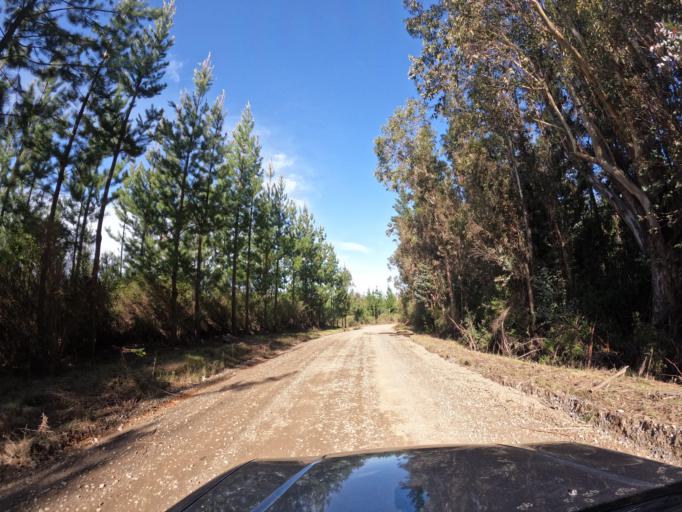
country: CL
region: Biobio
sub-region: Provincia de Biobio
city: La Laja
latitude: -37.0846
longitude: -72.7786
